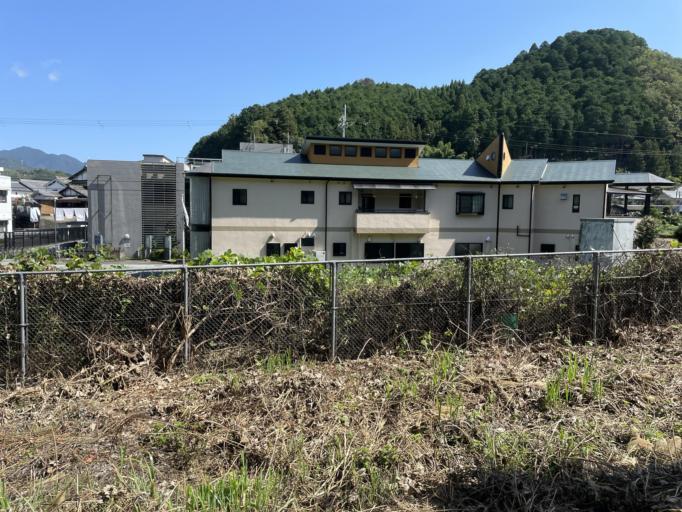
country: JP
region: Nara
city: Yoshino-cho
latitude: 34.3883
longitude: 135.8489
